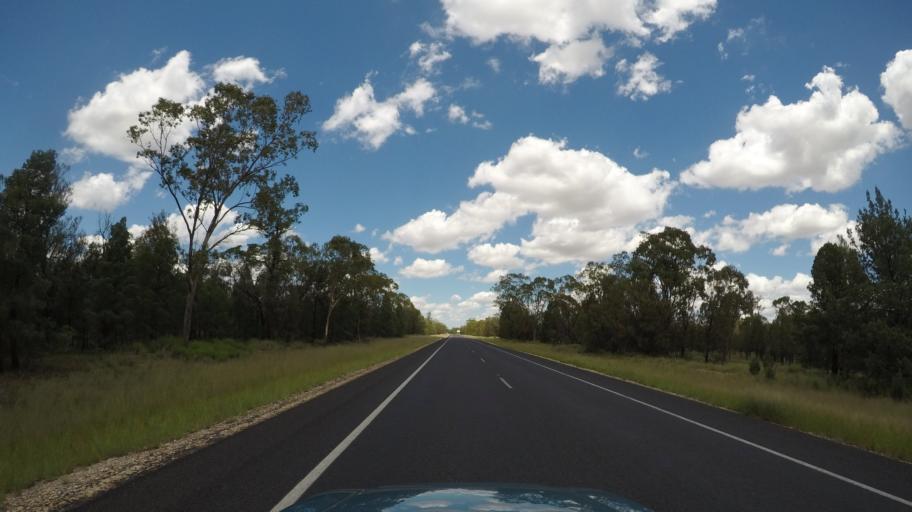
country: AU
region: Queensland
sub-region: Goondiwindi
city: Goondiwindi
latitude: -28.0682
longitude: 150.7549
